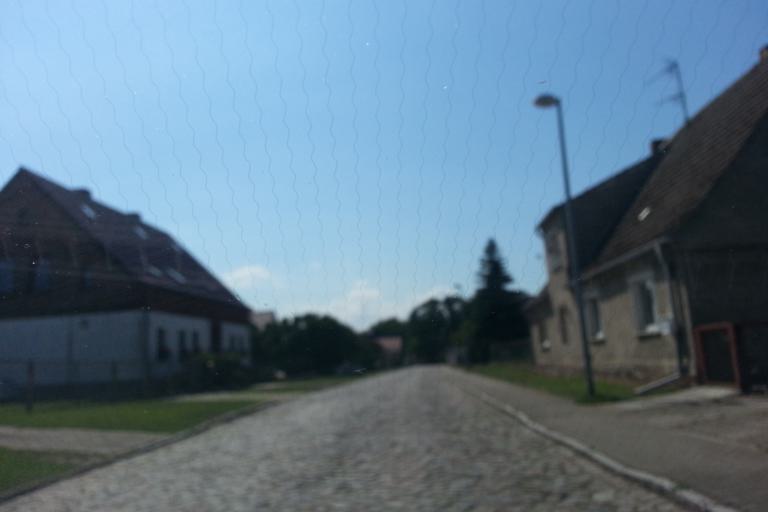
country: DE
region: Mecklenburg-Vorpommern
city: Ferdinandshof
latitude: 53.7039
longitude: 13.8364
